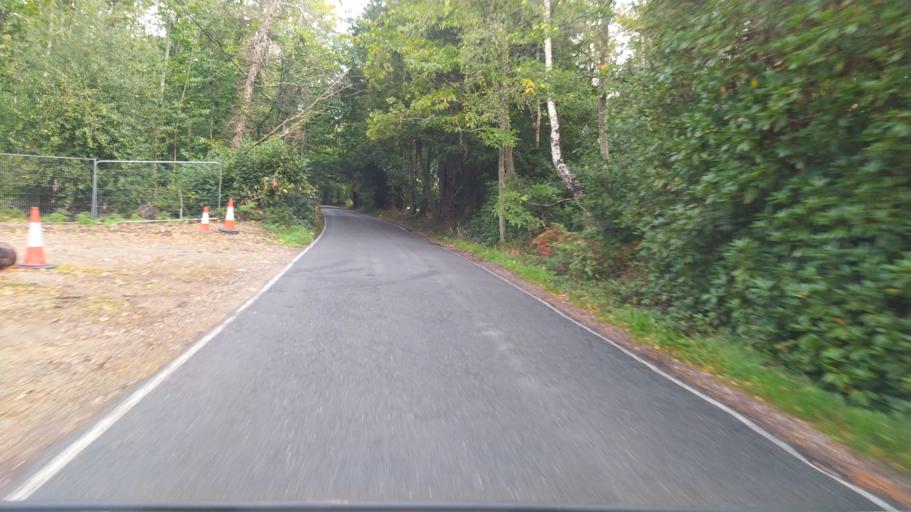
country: GB
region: England
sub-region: Hampshire
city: Romsey
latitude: 50.9837
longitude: -1.5313
